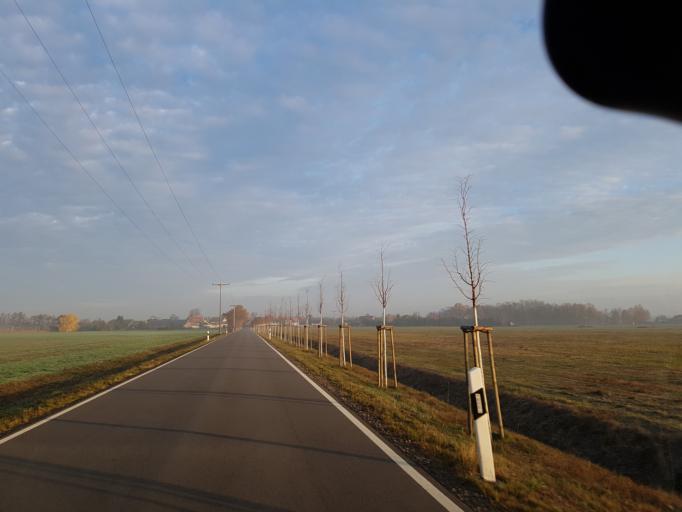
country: DE
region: Saxony-Anhalt
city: Elster
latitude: 51.8599
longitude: 12.8452
